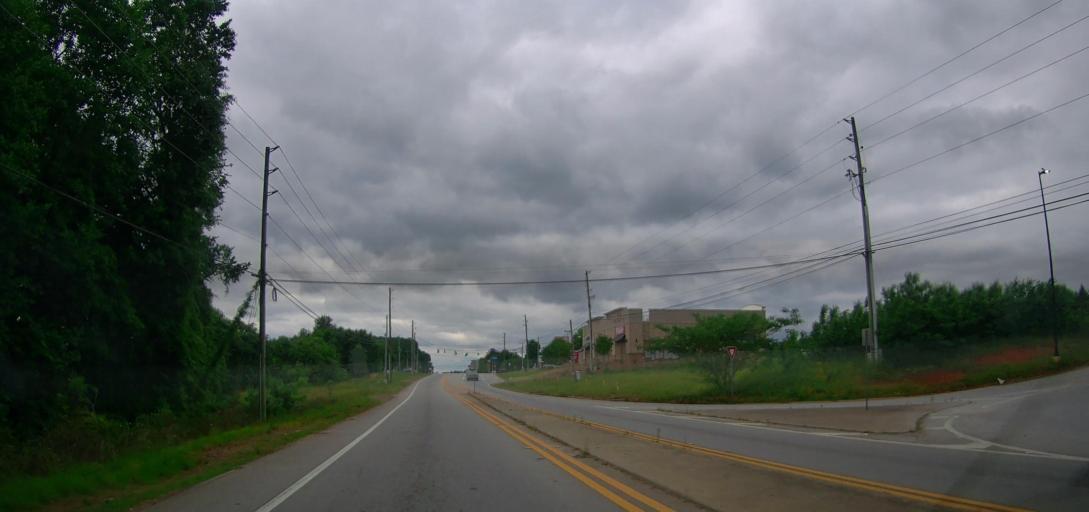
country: US
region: Georgia
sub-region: Walton County
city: Monroe
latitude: 33.7973
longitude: -83.7449
